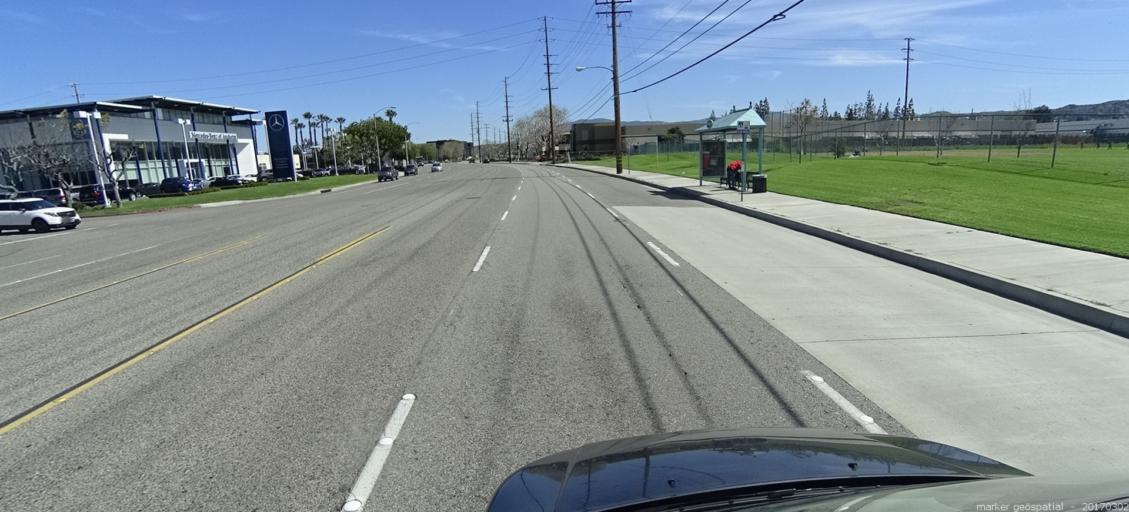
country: US
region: California
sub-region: Orange County
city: Yorba Linda
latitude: 33.8594
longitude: -117.7995
